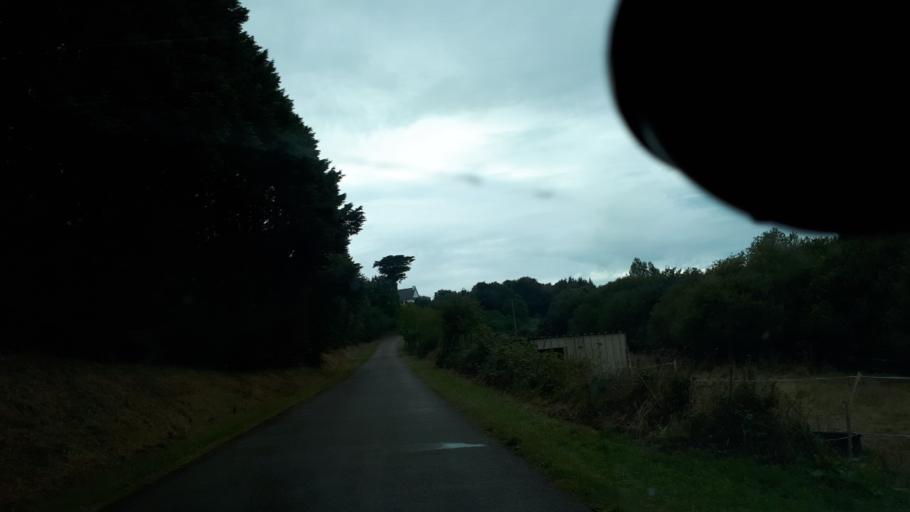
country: FR
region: Brittany
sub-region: Departement du Finistere
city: Pouldreuzic
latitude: 47.9635
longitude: -4.3925
